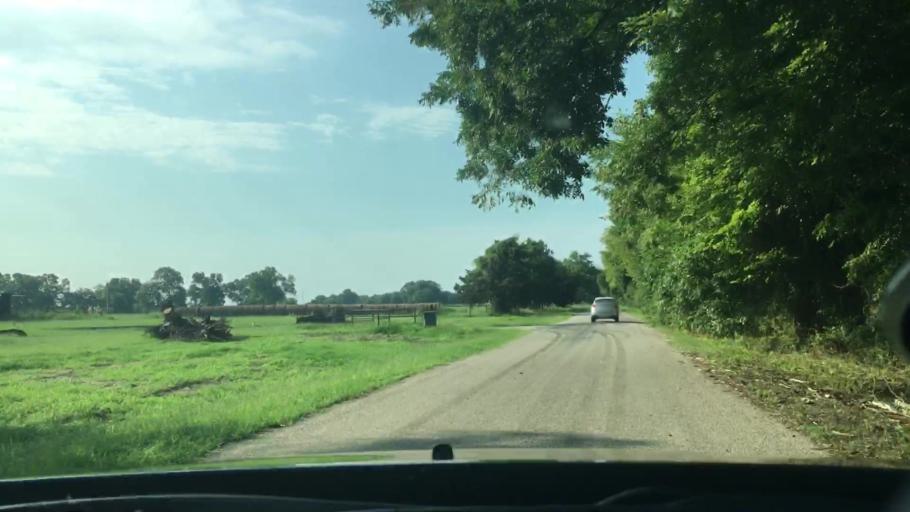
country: US
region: Oklahoma
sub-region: Johnston County
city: Tishomingo
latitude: 34.2117
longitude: -96.6691
